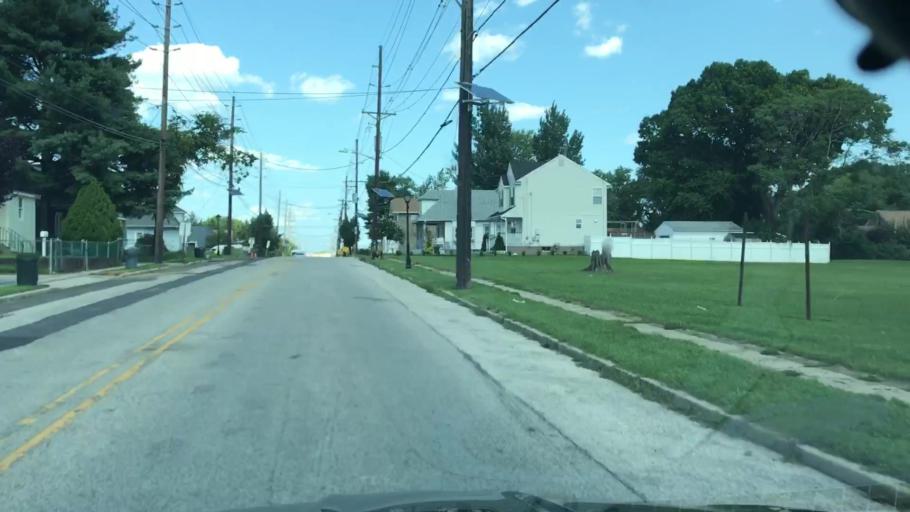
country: US
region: New Jersey
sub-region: Camden County
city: Pennsauken
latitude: 39.9834
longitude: -75.0502
